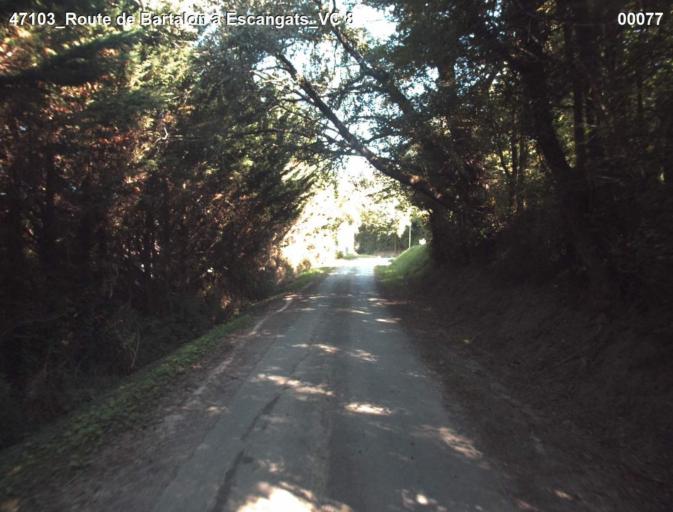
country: FR
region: Aquitaine
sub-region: Departement du Lot-et-Garonne
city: Nerac
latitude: 44.0936
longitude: 0.3157
